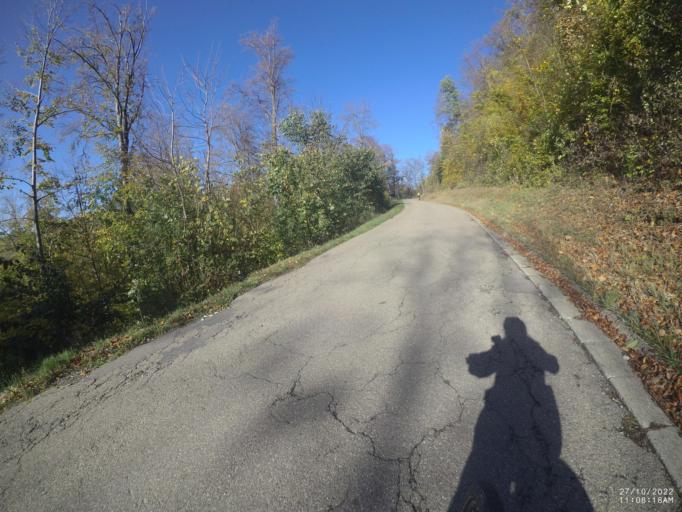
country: DE
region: Baden-Wuerttemberg
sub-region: Regierungsbezirk Stuttgart
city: Muhlhausen
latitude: 48.5667
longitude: 9.6845
